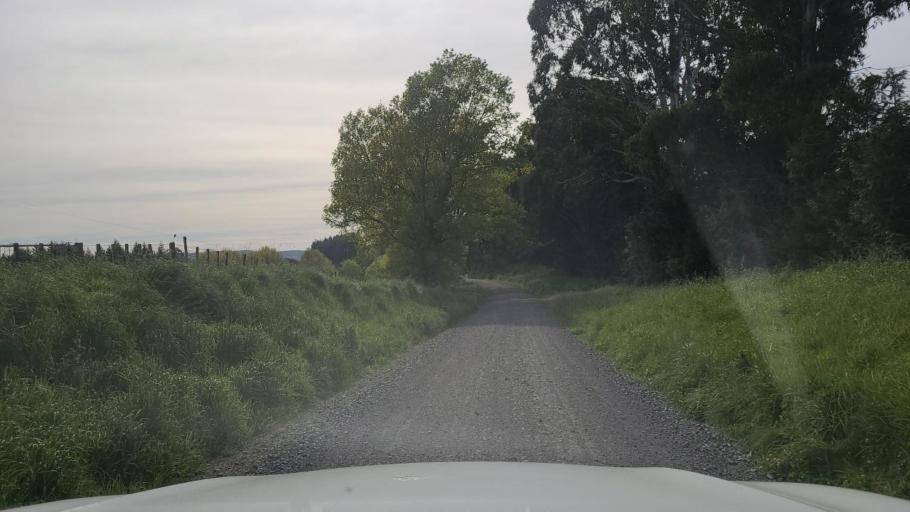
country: NZ
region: Hawke's Bay
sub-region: Napier City
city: Taradale
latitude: -39.3027
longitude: 176.6285
